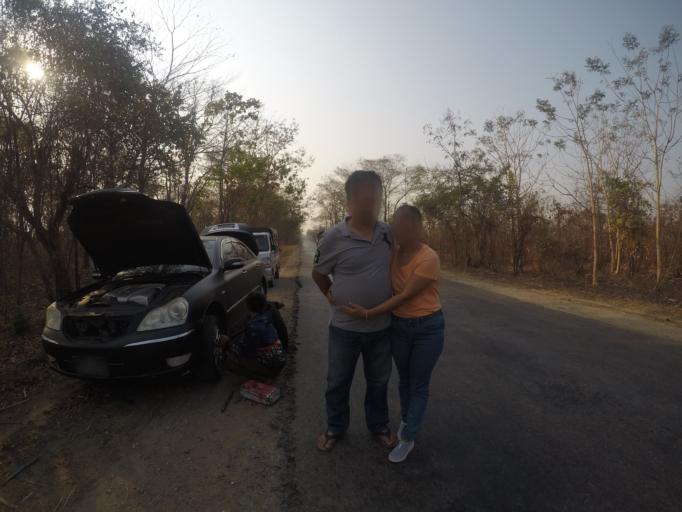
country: MM
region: Bago
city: Pyay
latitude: 18.9350
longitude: 95.2591
